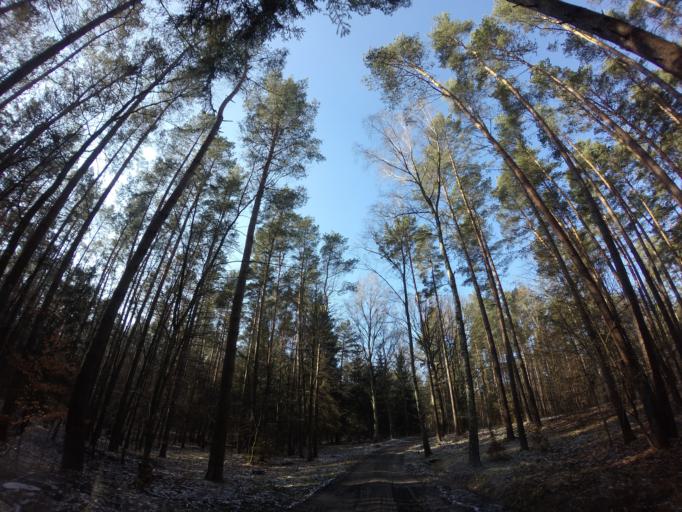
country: PL
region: West Pomeranian Voivodeship
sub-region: Powiat choszczenski
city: Pelczyce
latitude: 52.9684
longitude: 15.3475
